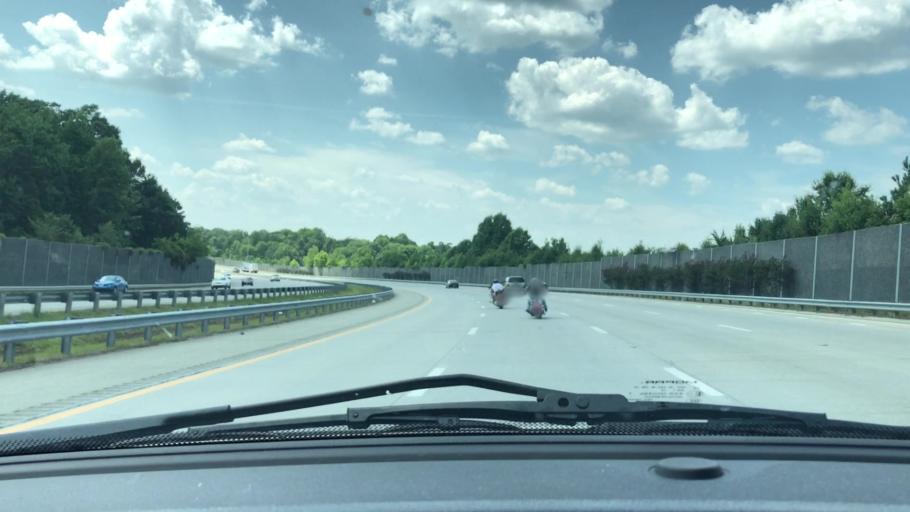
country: US
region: North Carolina
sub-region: Guilford County
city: Greensboro
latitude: 36.0191
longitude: -79.8543
